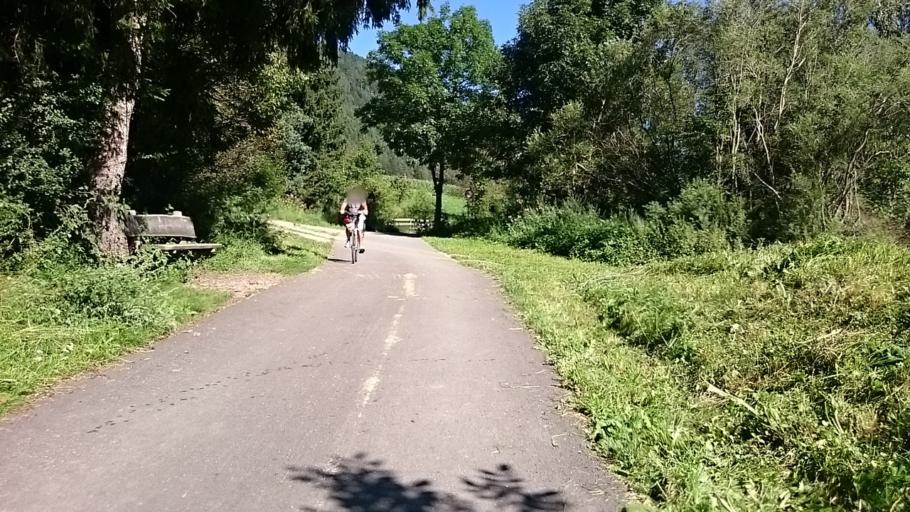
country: IT
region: Trentino-Alto Adige
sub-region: Bolzano
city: Perca
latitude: 46.7837
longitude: 12.0042
